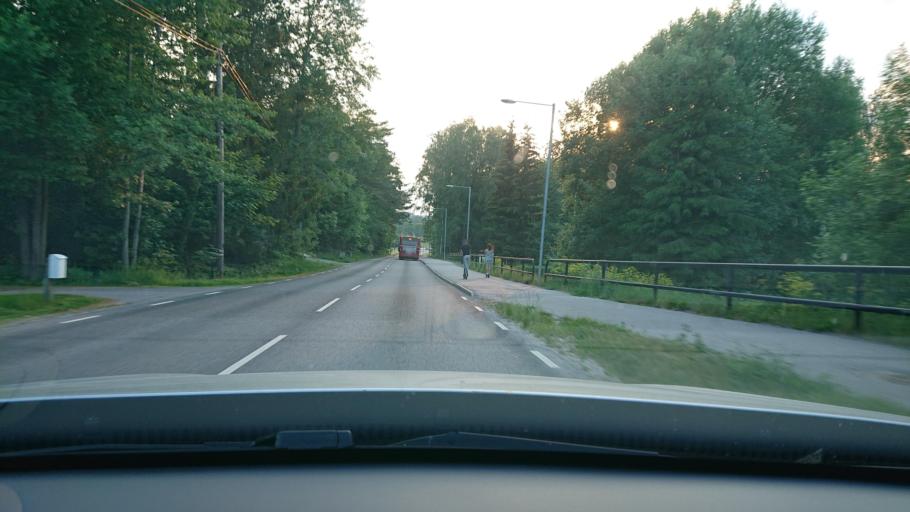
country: SE
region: Stockholm
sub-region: Vaxholms Kommun
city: Resaro
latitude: 59.4617
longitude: 18.3470
